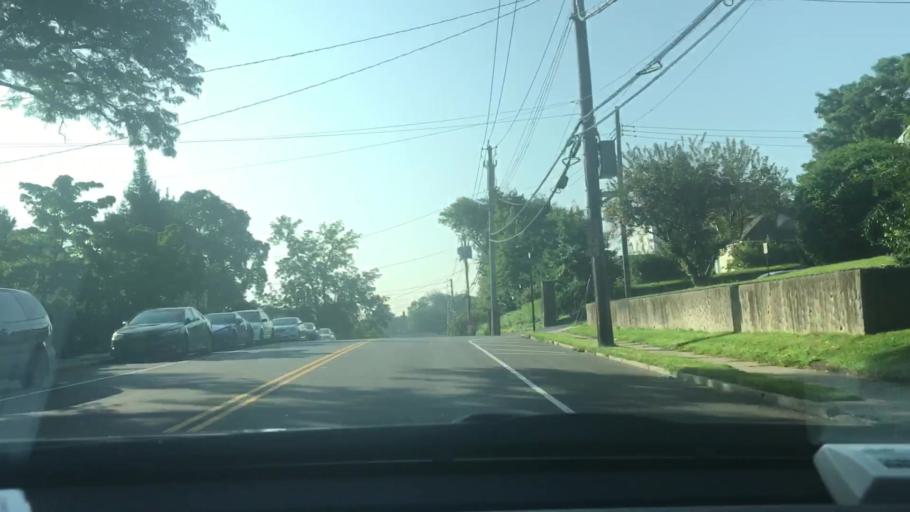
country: US
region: New York
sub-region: Westchester County
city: New Rochelle
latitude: 40.9131
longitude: -73.7763
